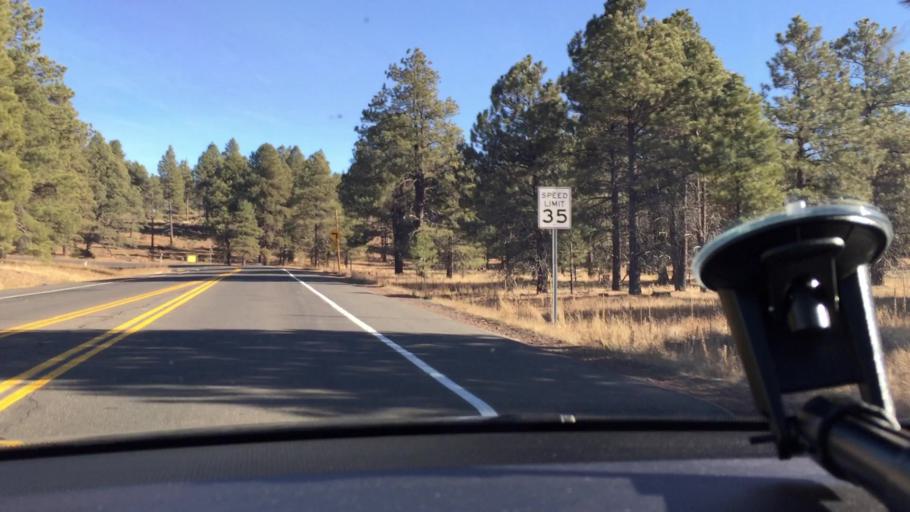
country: US
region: Arizona
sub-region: Coconino County
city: Kachina Village
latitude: 35.0897
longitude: -111.6844
